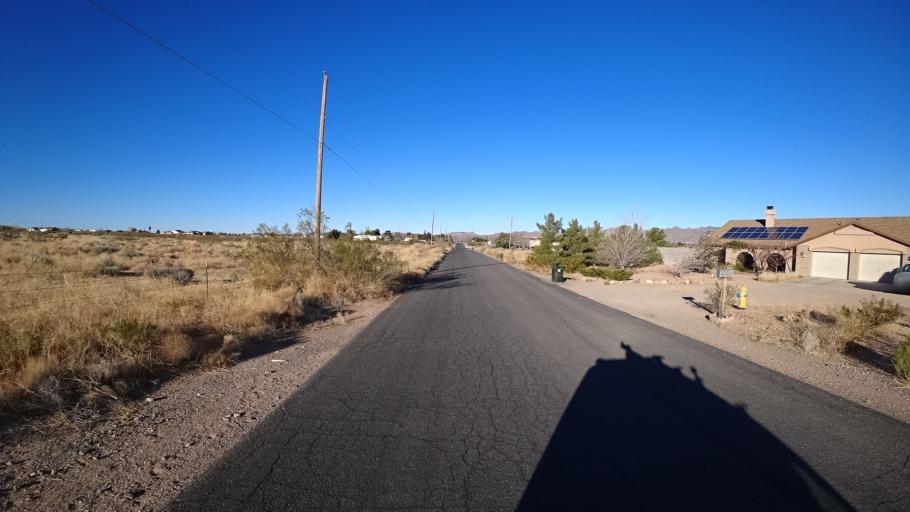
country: US
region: Arizona
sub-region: Mohave County
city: Kingman
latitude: 35.2031
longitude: -113.9948
